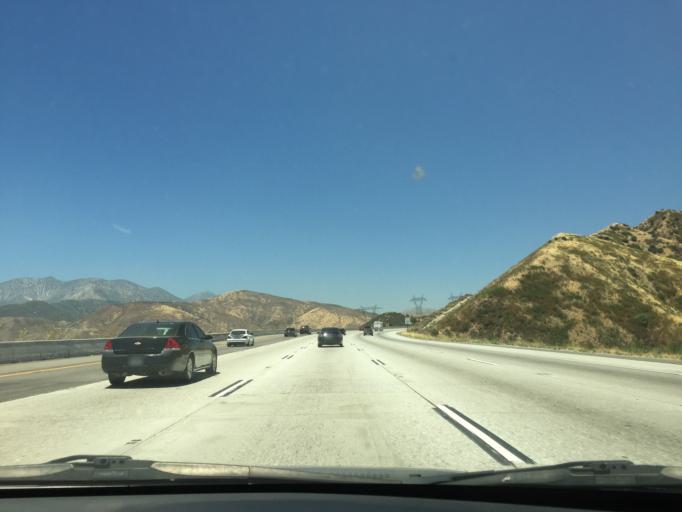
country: US
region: California
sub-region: San Bernardino County
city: Muscoy
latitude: 34.2507
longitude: -117.4442
